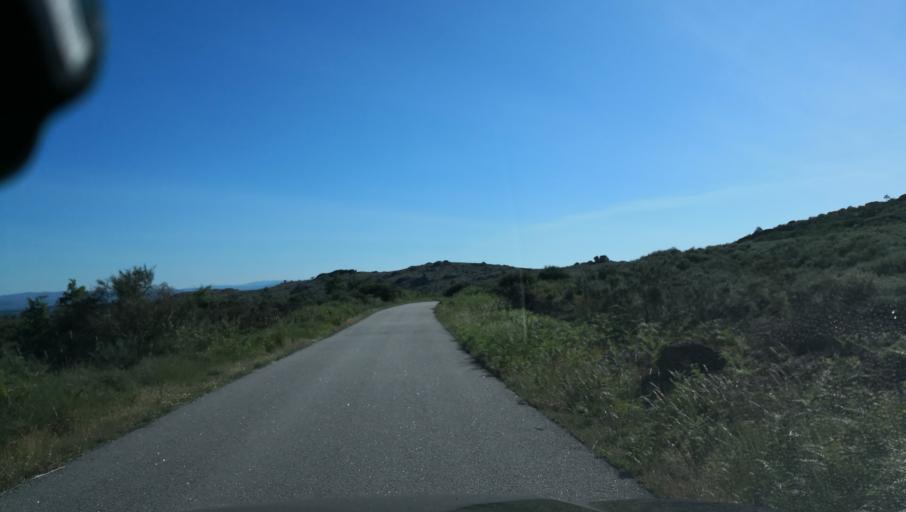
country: PT
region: Vila Real
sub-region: Sabrosa
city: Sabrosa
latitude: 41.2969
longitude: -7.6244
